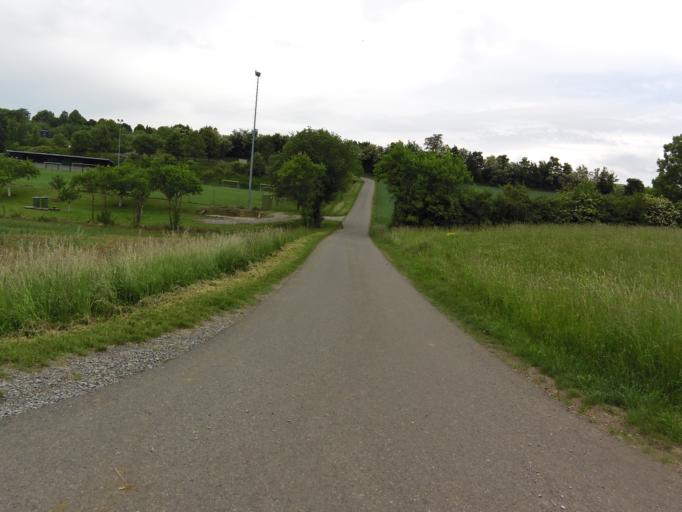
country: DE
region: Bavaria
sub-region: Regierungsbezirk Unterfranken
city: Waldbrunn
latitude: 49.7093
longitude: 9.7917
